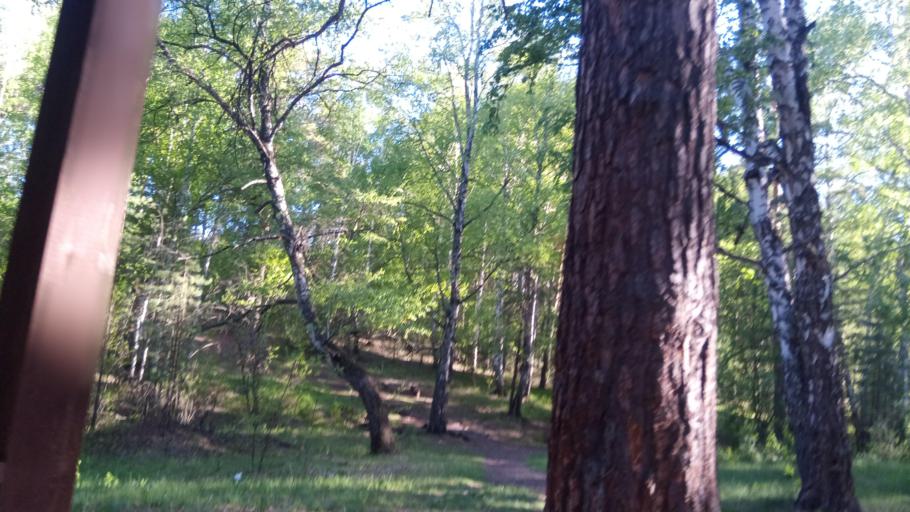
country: RU
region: Chelyabinsk
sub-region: Gorod Chelyabinsk
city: Chelyabinsk
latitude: 55.1411
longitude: 61.3388
